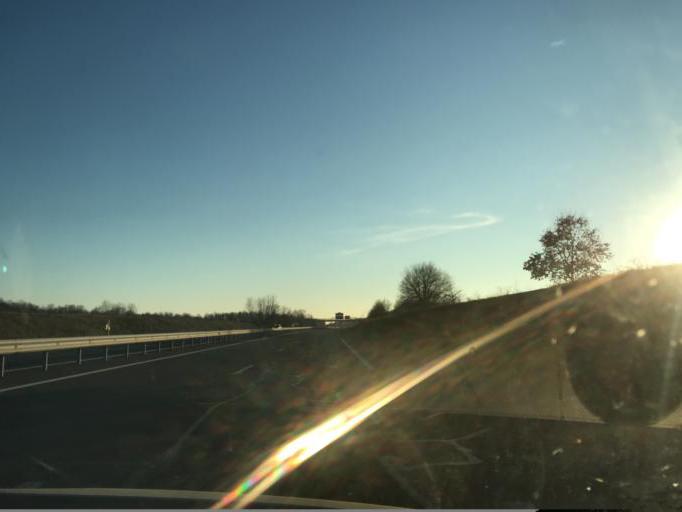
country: FR
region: Bourgogne
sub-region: Departement de l'Yonne
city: Egriselles-le-Bocage
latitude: 48.1522
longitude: 3.1690
